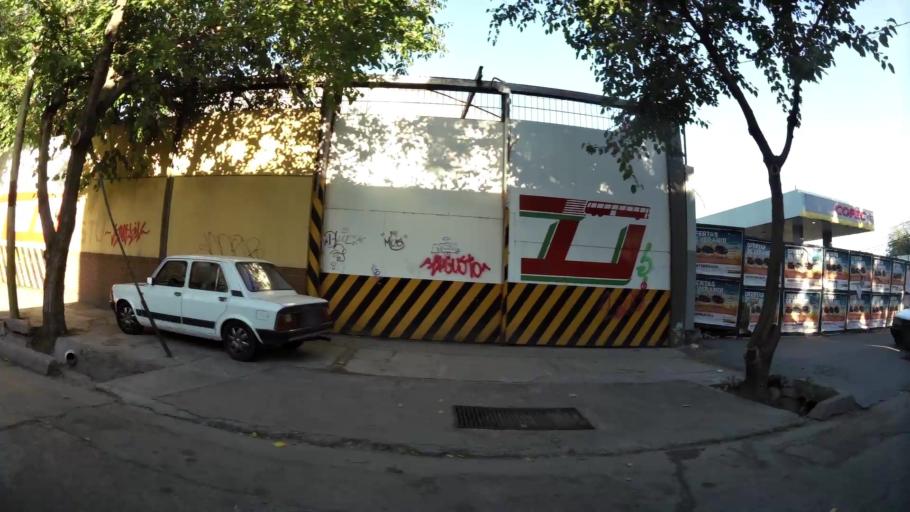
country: AR
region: Mendoza
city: Las Heras
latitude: -32.8671
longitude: -68.8291
